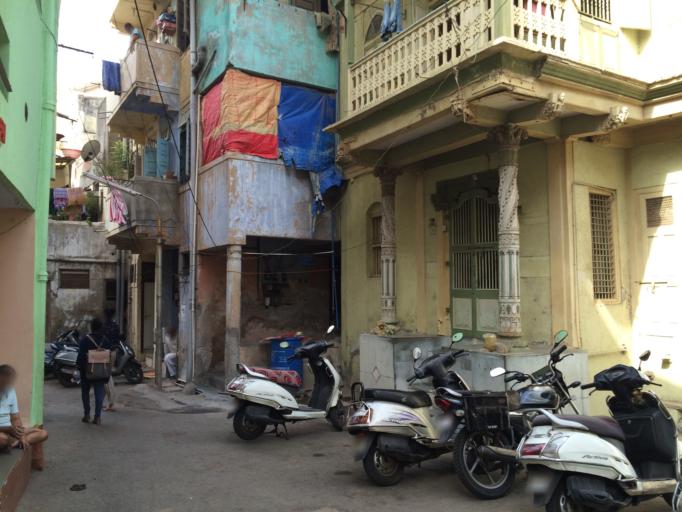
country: IN
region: Gujarat
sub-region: Ahmadabad
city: Ahmedabad
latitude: 23.0226
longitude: 72.5912
